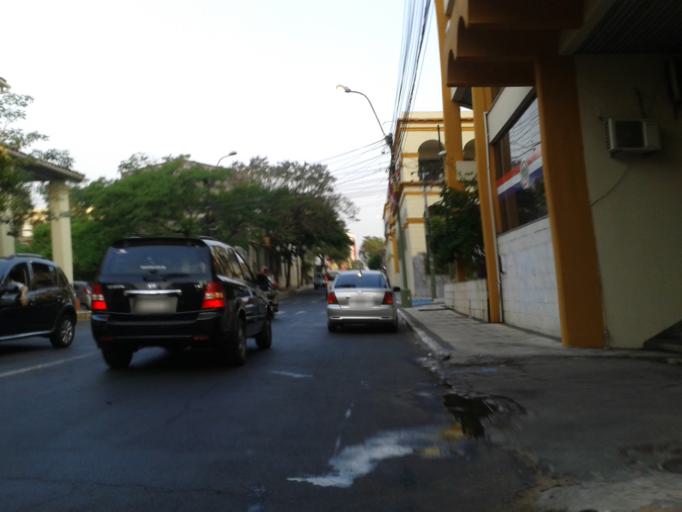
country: PY
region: Asuncion
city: Asuncion
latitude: -25.2819
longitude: -57.6324
